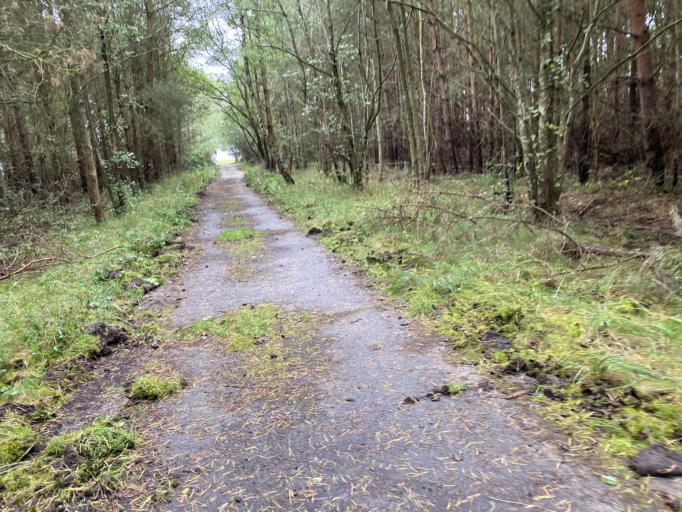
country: DE
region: Mecklenburg-Vorpommern
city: Ostseebad Binz
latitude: 54.4433
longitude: 13.5584
